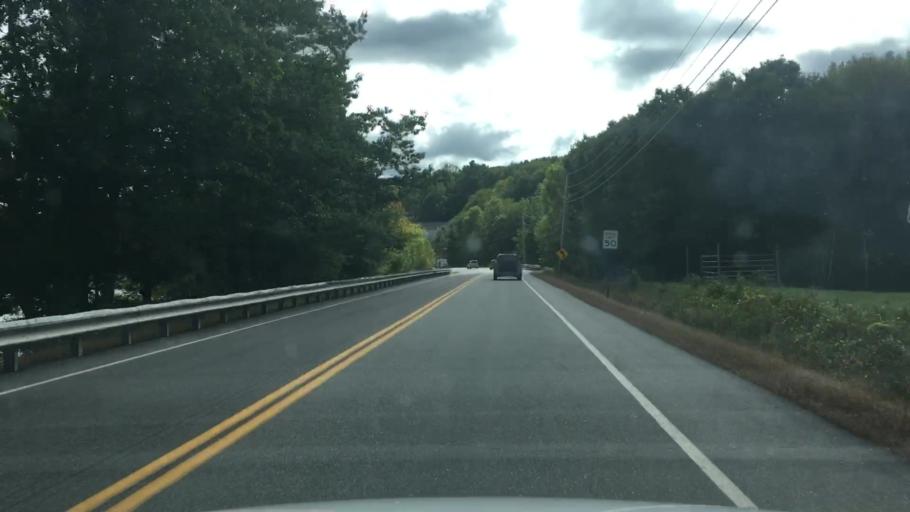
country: US
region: Maine
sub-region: Androscoggin County
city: Lisbon
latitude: 44.0109
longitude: -70.1680
